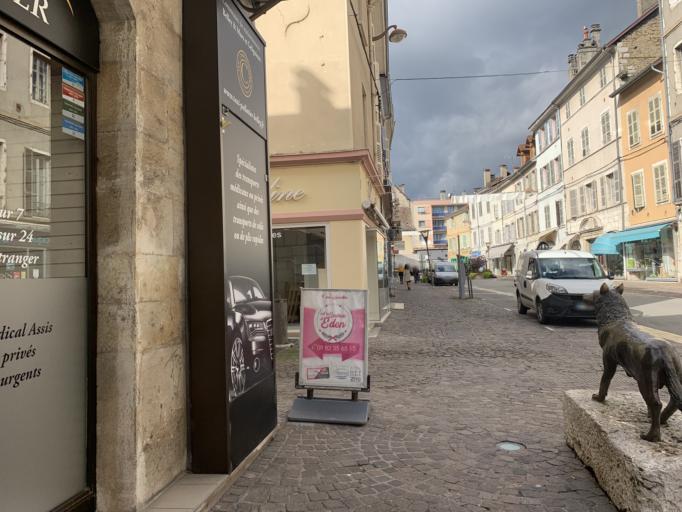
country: FR
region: Rhone-Alpes
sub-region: Departement de l'Ain
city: Belley
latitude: 45.7601
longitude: 5.6877
